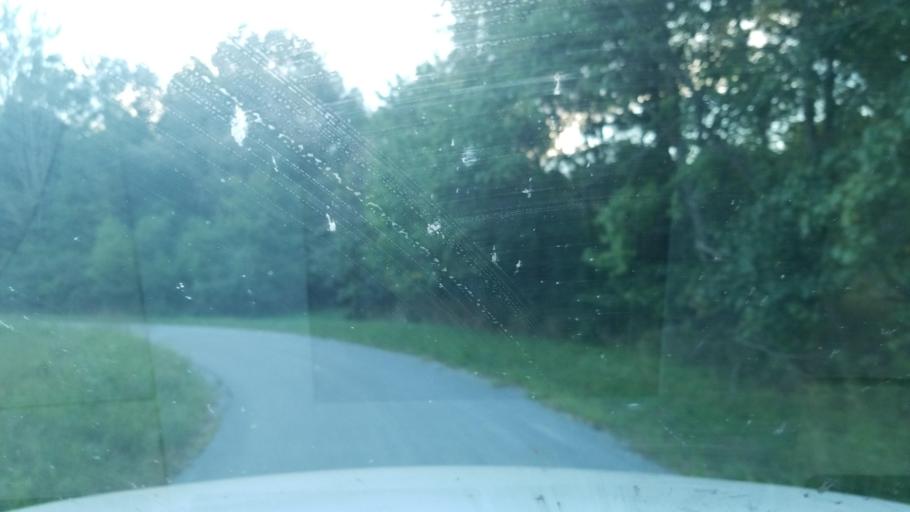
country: US
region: Illinois
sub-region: Saline County
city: Carrier Mills
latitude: 37.7903
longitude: -88.7049
